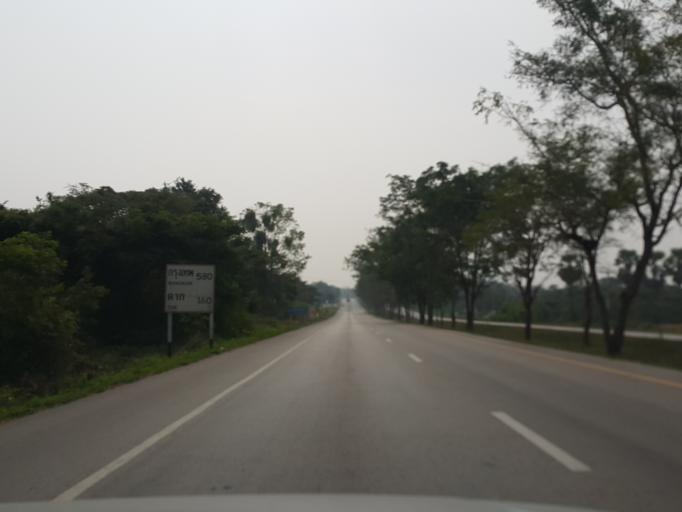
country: TH
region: Lampang
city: Ko Kha
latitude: 18.1386
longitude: 99.3908
